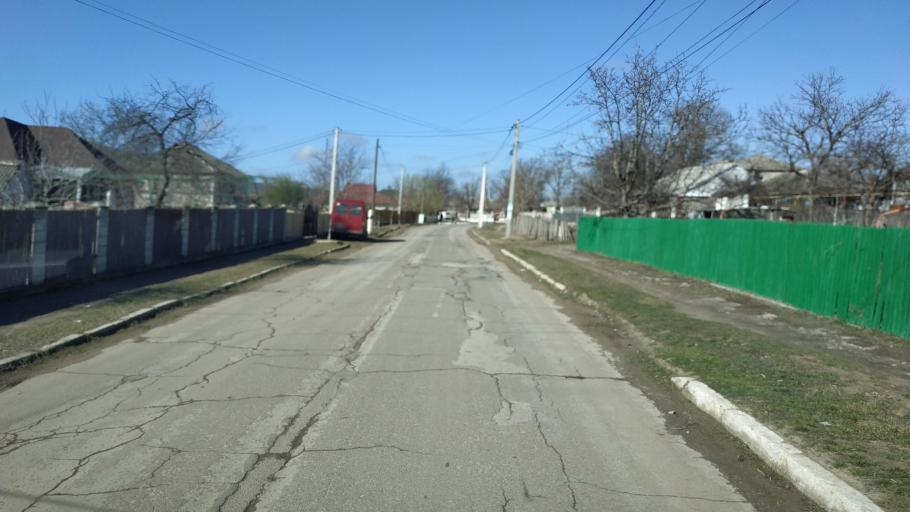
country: MD
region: Hincesti
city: Hincesti
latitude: 46.9724
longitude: 28.5804
